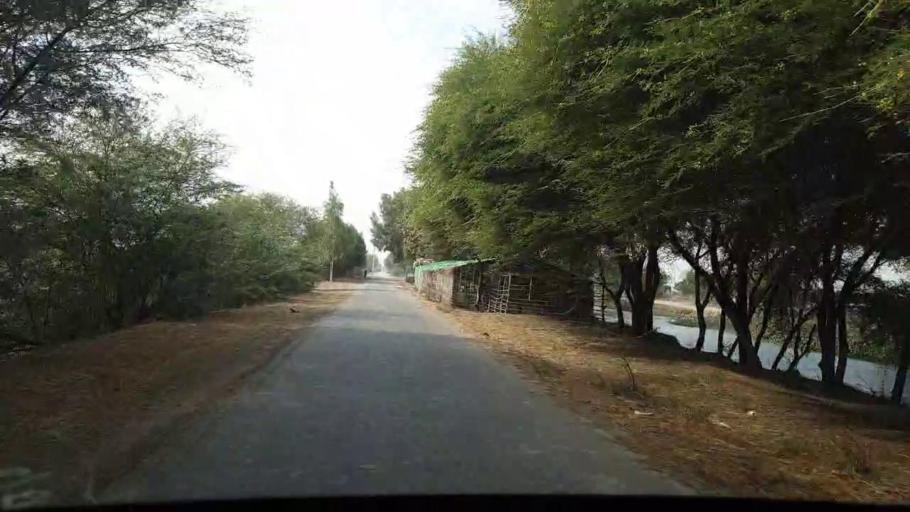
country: PK
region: Sindh
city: Chuhar Jamali
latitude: 24.3888
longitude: 67.9483
